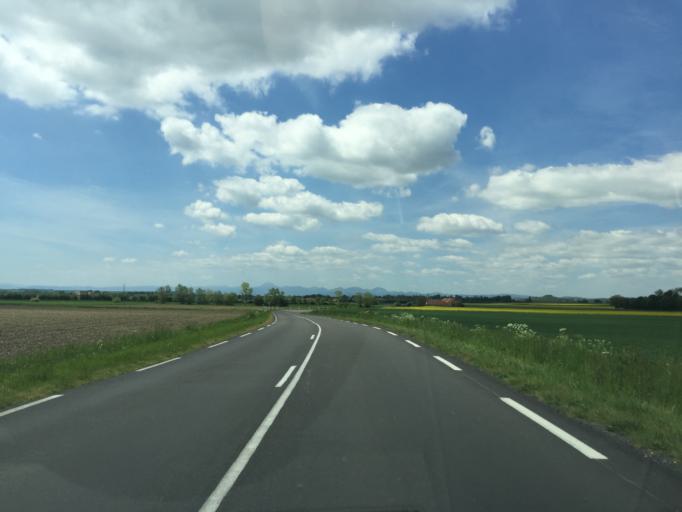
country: FR
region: Auvergne
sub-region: Departement du Puy-de-Dome
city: Aigueperse
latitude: 46.0542
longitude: 3.2739
